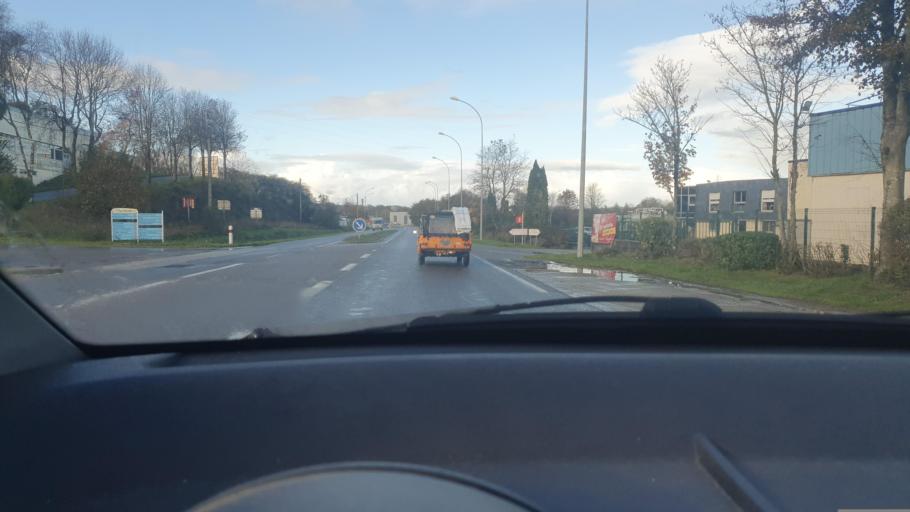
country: FR
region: Brittany
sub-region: Departement du Finistere
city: Briec
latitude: 48.1003
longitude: -4.0207
